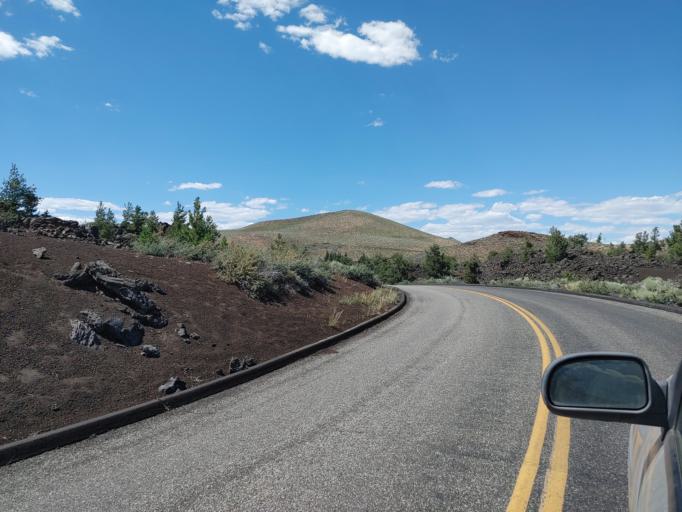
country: US
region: Idaho
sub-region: Butte County
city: Arco
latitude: 43.4583
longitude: -113.5562
